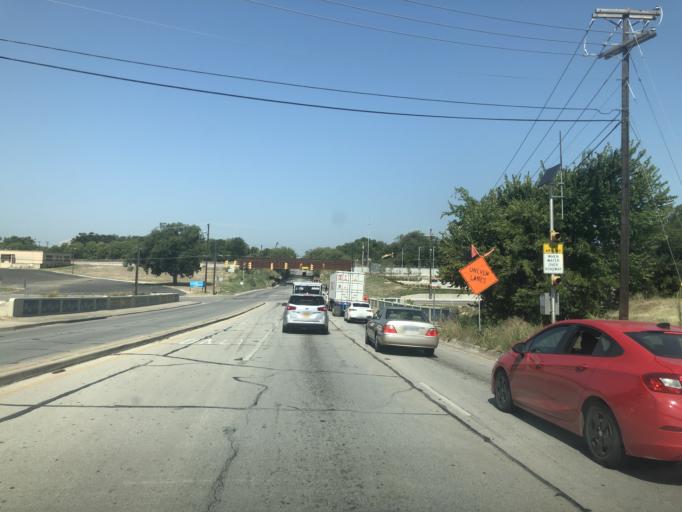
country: US
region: Texas
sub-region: Tarrant County
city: River Oaks
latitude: 32.7952
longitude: -97.3360
